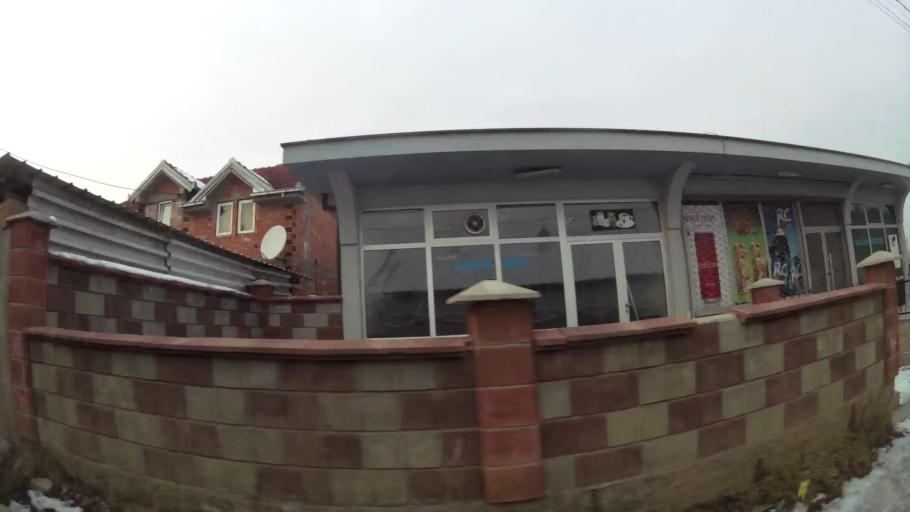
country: MK
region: Suto Orizari
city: Suto Orizare
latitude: 42.0340
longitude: 21.4191
